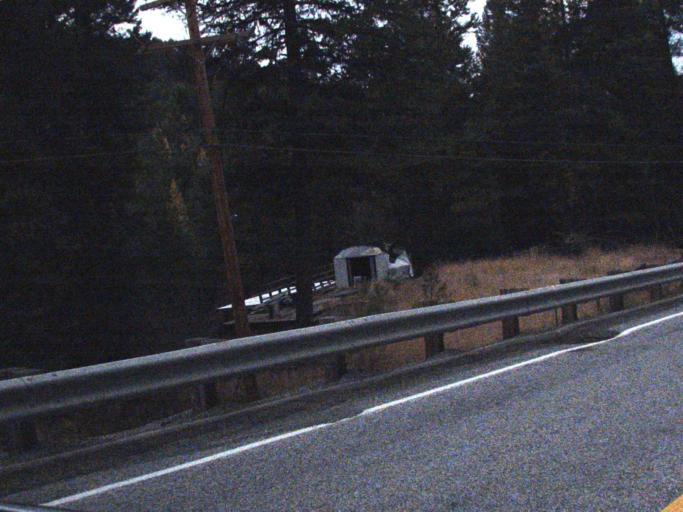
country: US
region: Washington
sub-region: Ferry County
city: Republic
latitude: 48.6409
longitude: -118.6816
